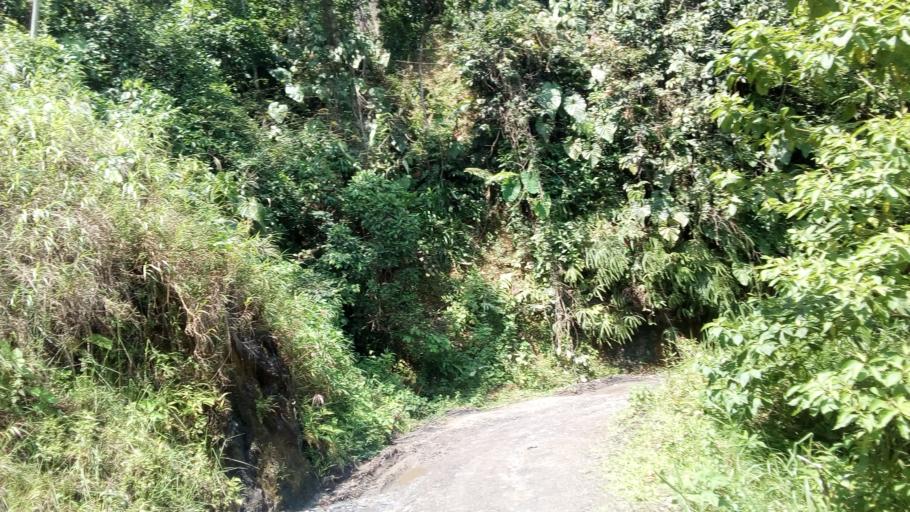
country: CO
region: Boyaca
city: Otanche
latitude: 5.6259
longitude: -74.2365
